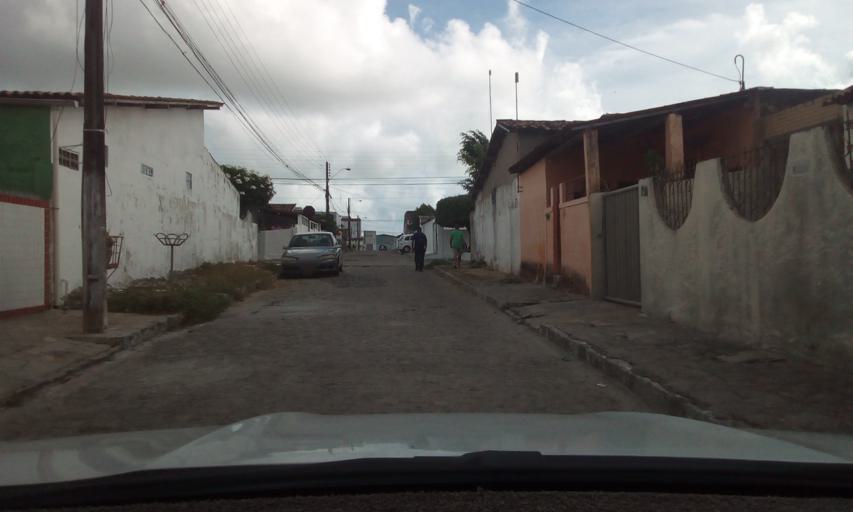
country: BR
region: Paraiba
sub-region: Joao Pessoa
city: Joao Pessoa
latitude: -7.1118
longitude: -34.8670
